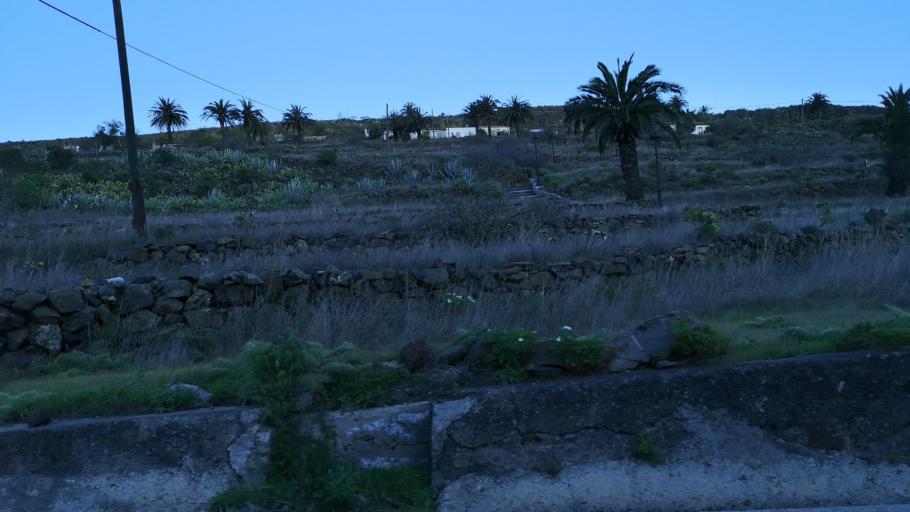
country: ES
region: Canary Islands
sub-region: Provincia de Santa Cruz de Tenerife
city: Alajero
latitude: 28.0681
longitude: -17.2387
